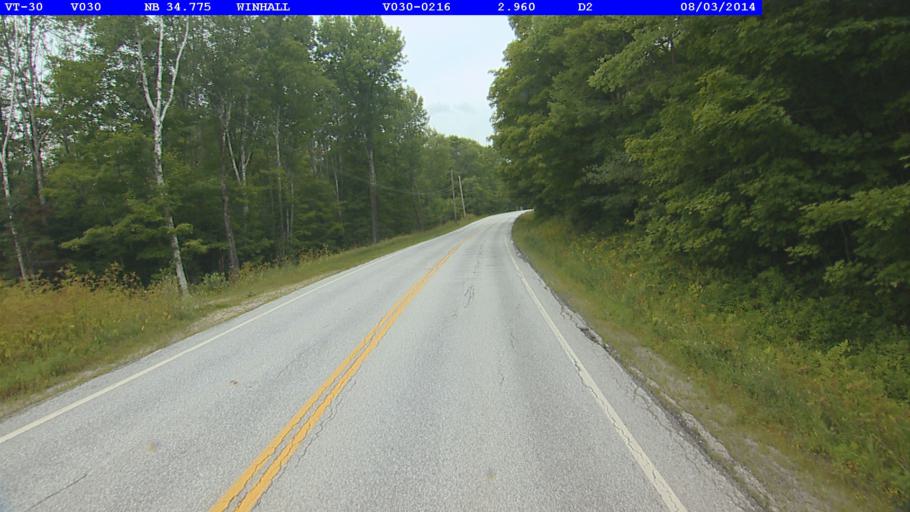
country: US
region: Vermont
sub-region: Bennington County
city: Manchester Center
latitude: 43.1563
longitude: -72.9195
